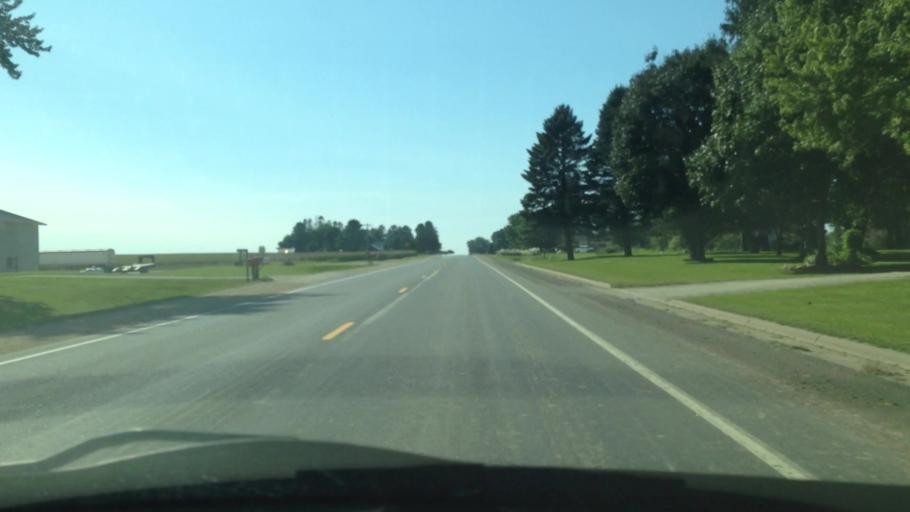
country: US
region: Minnesota
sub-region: Winona County
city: Lewiston
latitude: 43.9696
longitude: -91.8219
